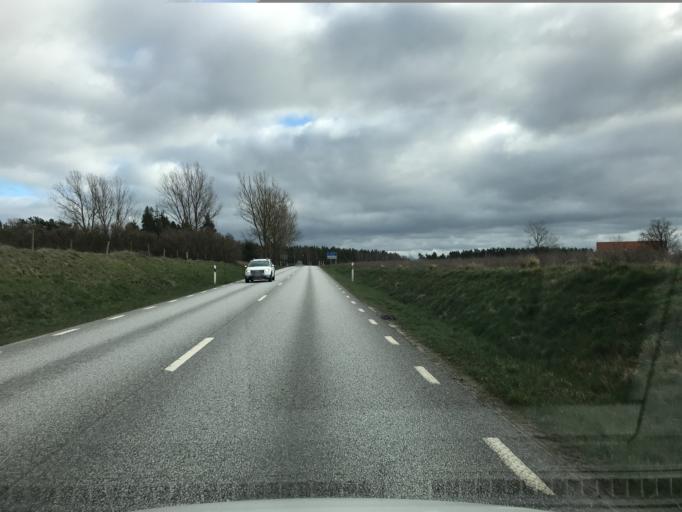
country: SE
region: Skane
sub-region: Kristianstads Kommun
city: Norra Asum
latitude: 55.9367
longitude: 14.0731
